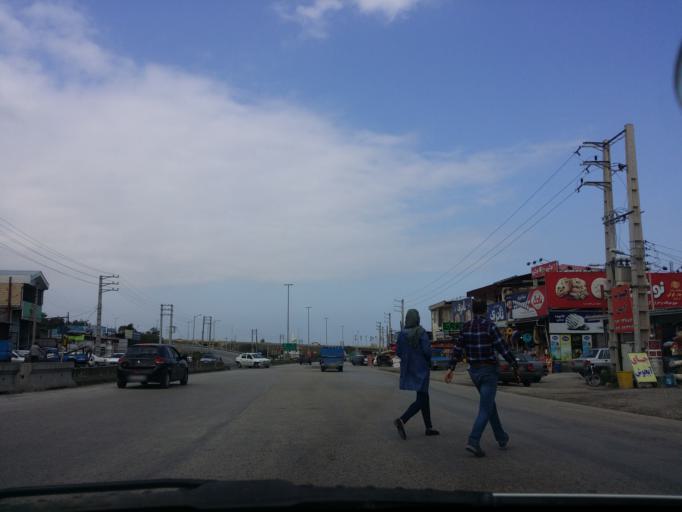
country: IR
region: Mazandaran
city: Chalus
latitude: 36.6491
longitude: 51.4087
